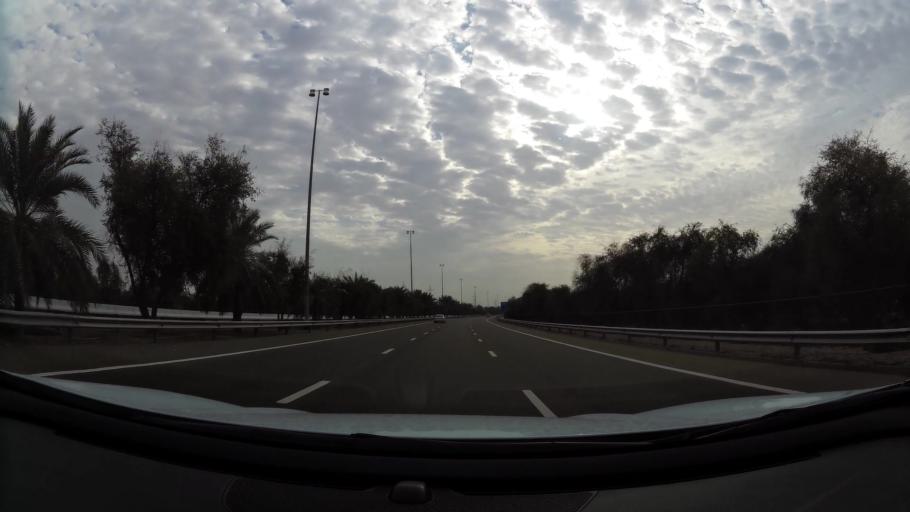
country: AE
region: Abu Dhabi
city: Al Ain
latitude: 24.1780
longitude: 55.1919
